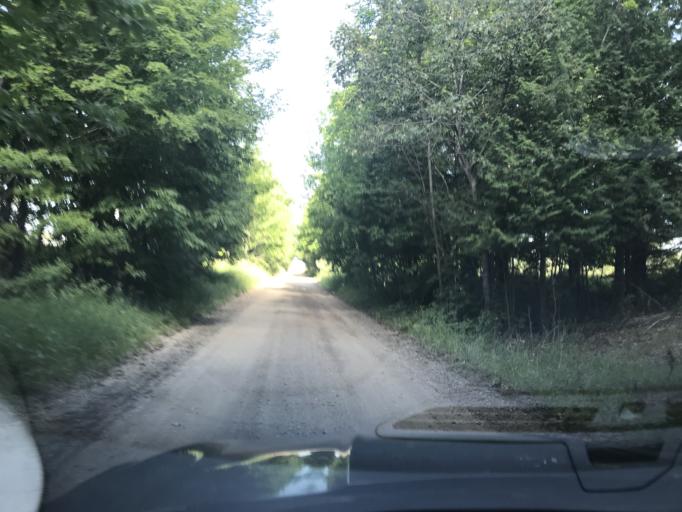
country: US
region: Michigan
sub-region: Cheboygan County
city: Cheboygan
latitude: 45.6216
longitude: -84.6741
